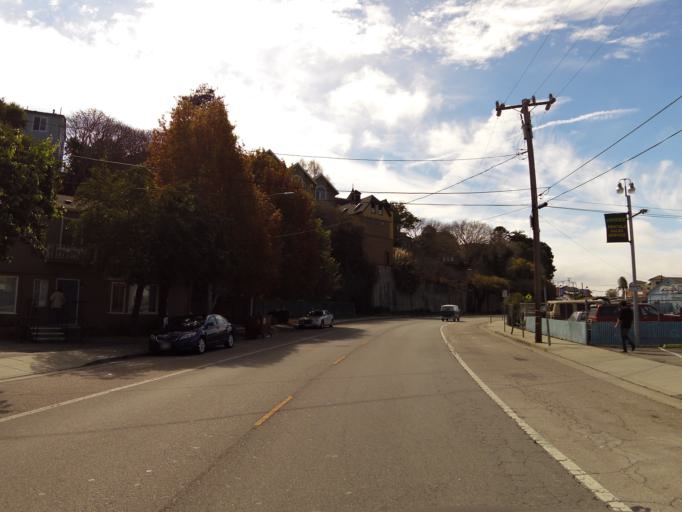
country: US
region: California
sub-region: Santa Cruz County
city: Santa Cruz
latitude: 36.9678
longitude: -122.0235
